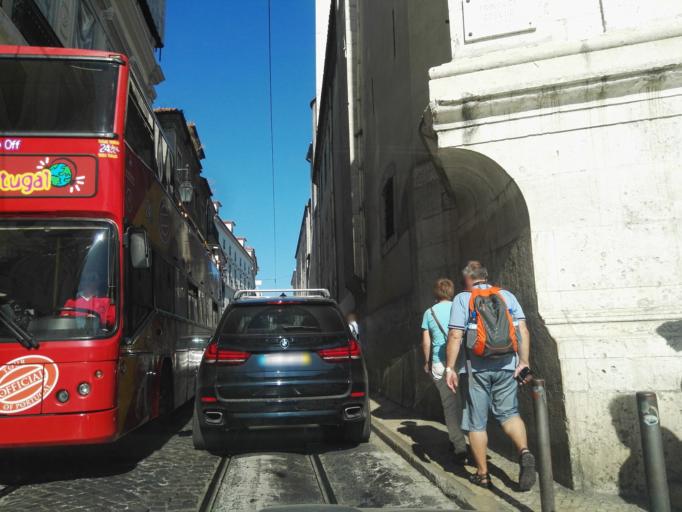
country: PT
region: Lisbon
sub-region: Lisbon
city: Lisbon
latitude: 38.7133
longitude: -9.1435
